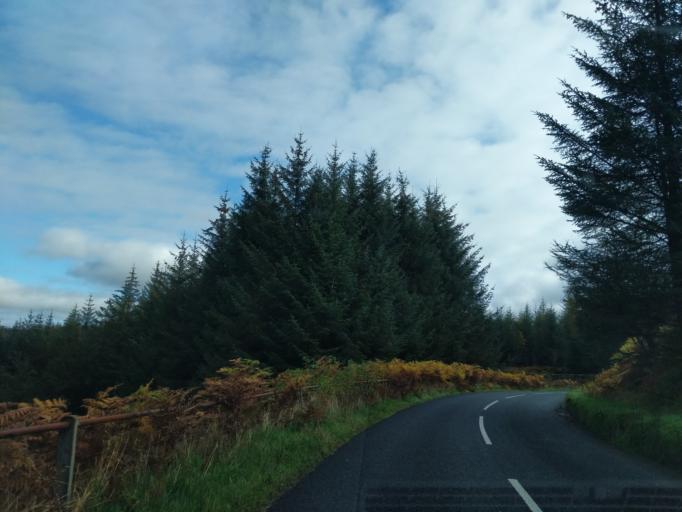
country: GB
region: Scotland
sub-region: Dumfries and Galloway
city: Castle Douglas
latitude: 55.1301
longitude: -4.0624
